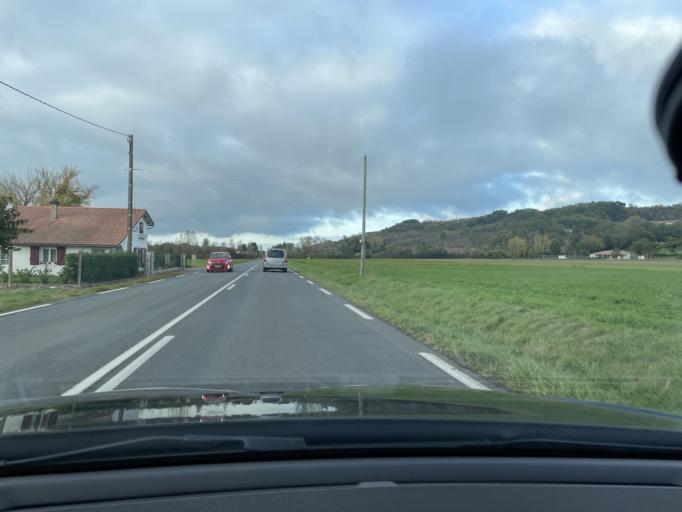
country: FR
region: Aquitaine
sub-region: Departement du Lot-et-Garonne
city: Casteljaloux
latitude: 44.3443
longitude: 0.1075
